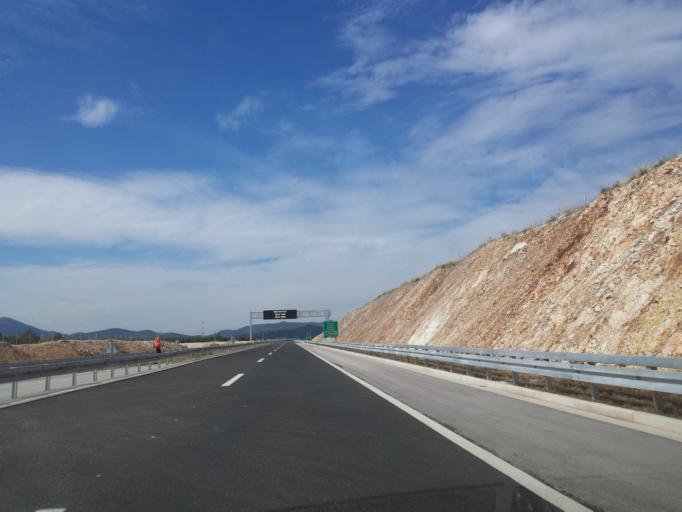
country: BA
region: Federation of Bosnia and Herzegovina
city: Capljina
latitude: 43.1538
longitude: 17.6228
